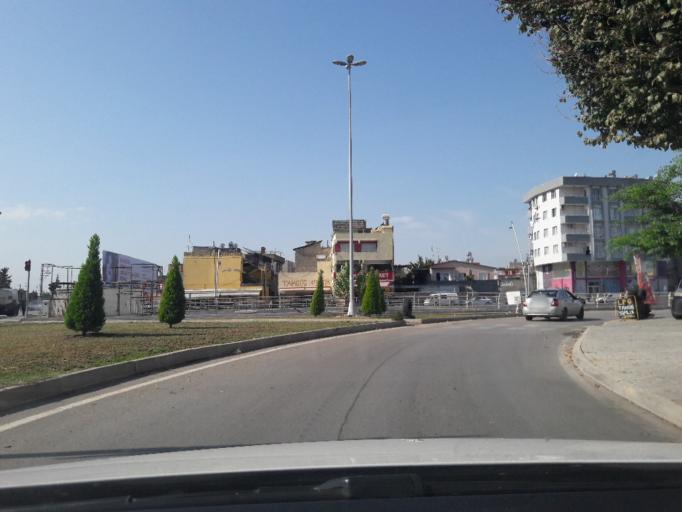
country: TR
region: Adana
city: Seyhan
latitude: 36.9980
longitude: 35.3018
